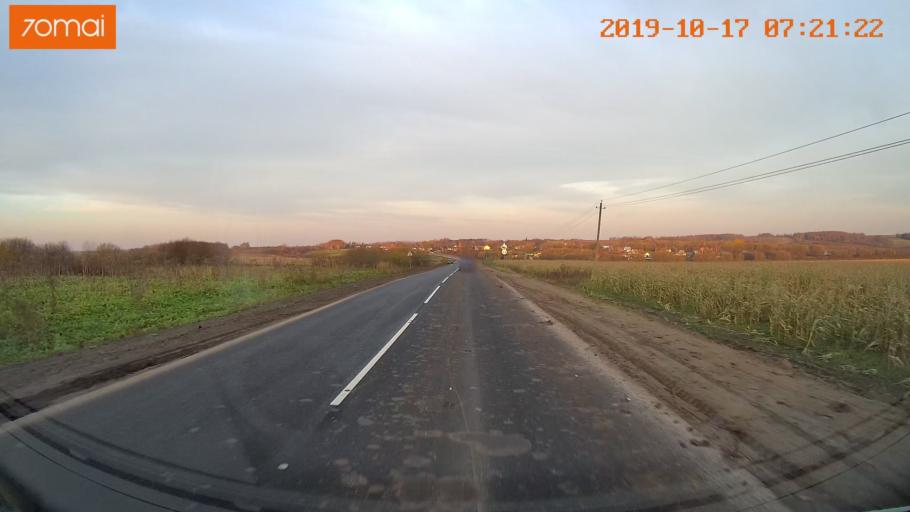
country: RU
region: Ivanovo
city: Gavrilov Posad
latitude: 56.3464
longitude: 40.1623
